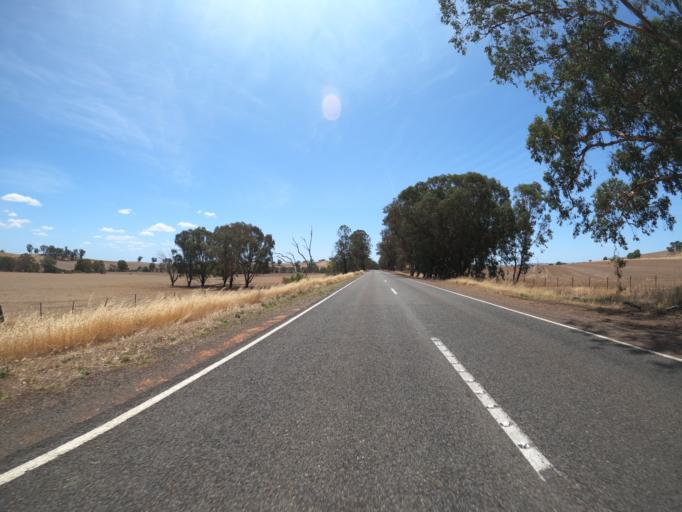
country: AU
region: Victoria
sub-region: Benalla
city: Benalla
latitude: -36.3407
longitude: 145.9590
